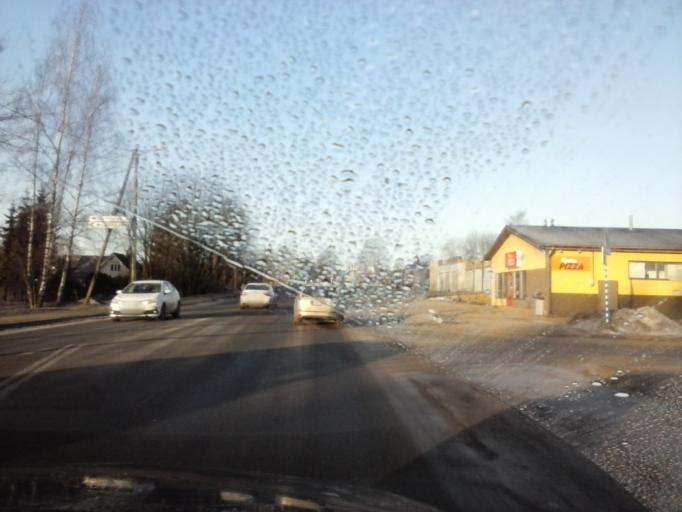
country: EE
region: Tartu
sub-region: Tartu linn
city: Tartu
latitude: 58.3552
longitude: 26.7129
